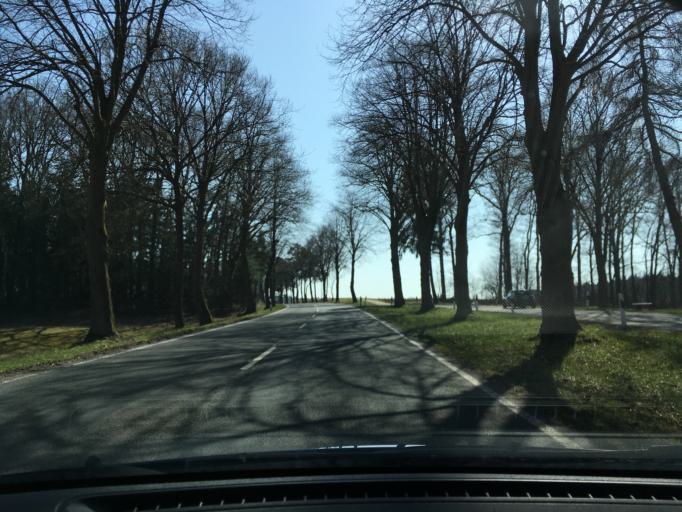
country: DE
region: Lower Saxony
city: Wriedel
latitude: 53.0714
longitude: 10.2848
